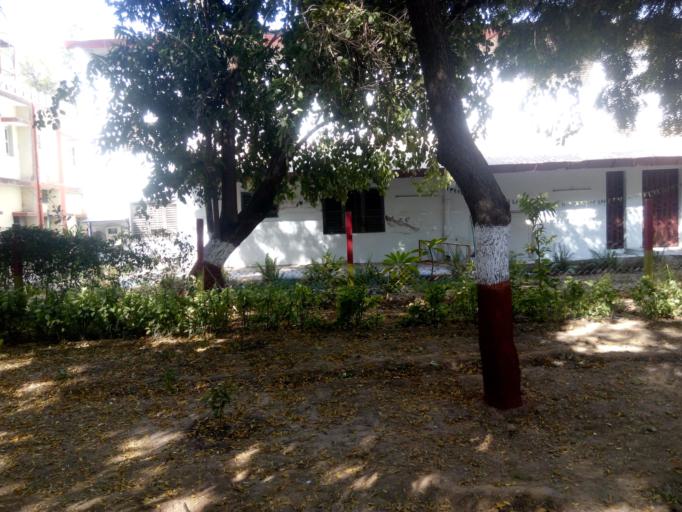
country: IN
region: Gujarat
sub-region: Ahmadabad
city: Ahmedabad
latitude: 23.0422
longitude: 72.5700
